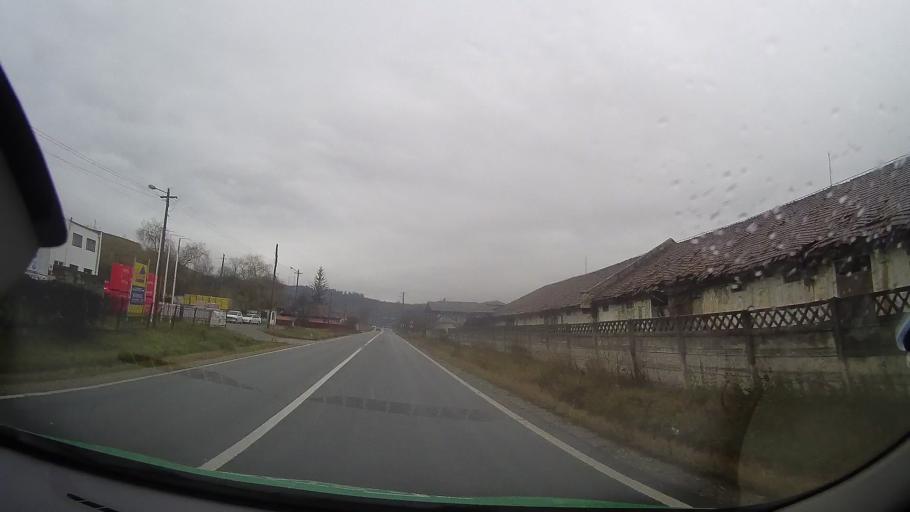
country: RO
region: Bistrita-Nasaud
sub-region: Comuna Teaca
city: Teaca
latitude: 46.9167
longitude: 24.4949
